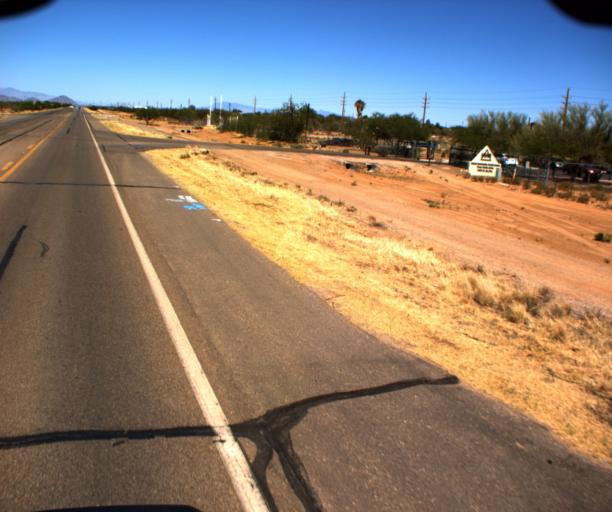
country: US
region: Arizona
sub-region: Pima County
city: Three Points
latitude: 32.0787
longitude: -111.3082
